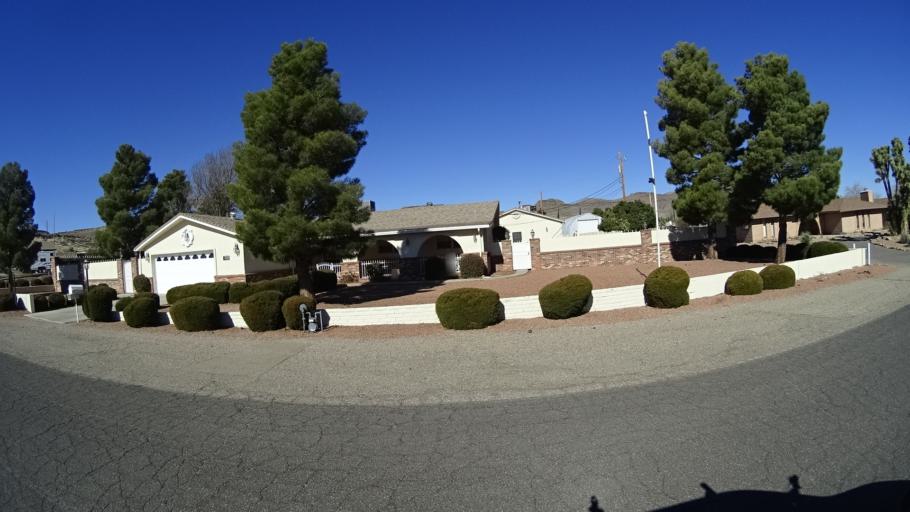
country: US
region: Arizona
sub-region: Mohave County
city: New Kingman-Butler
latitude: 35.2301
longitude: -114.0447
